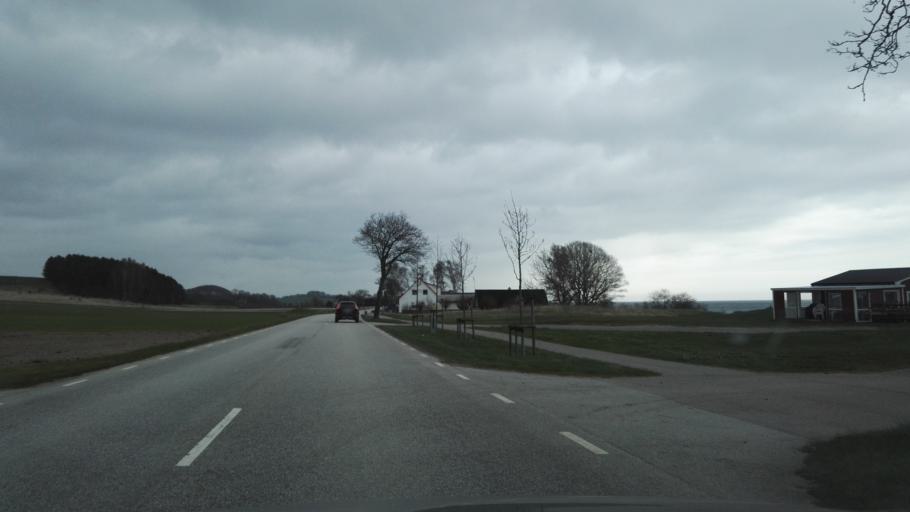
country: SE
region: Skane
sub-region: Skurups Kommun
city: Skivarp
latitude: 55.4184
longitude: 13.6423
